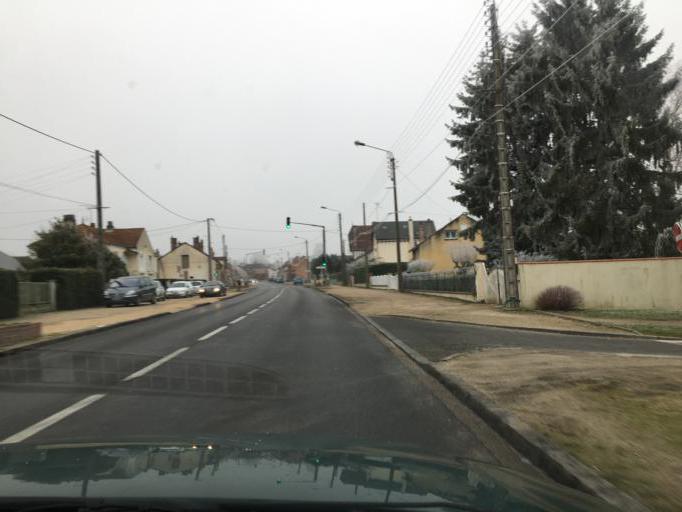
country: FR
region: Centre
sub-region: Departement du Loiret
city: La Ferte-Saint-Aubin
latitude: 47.7165
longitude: 1.9413
